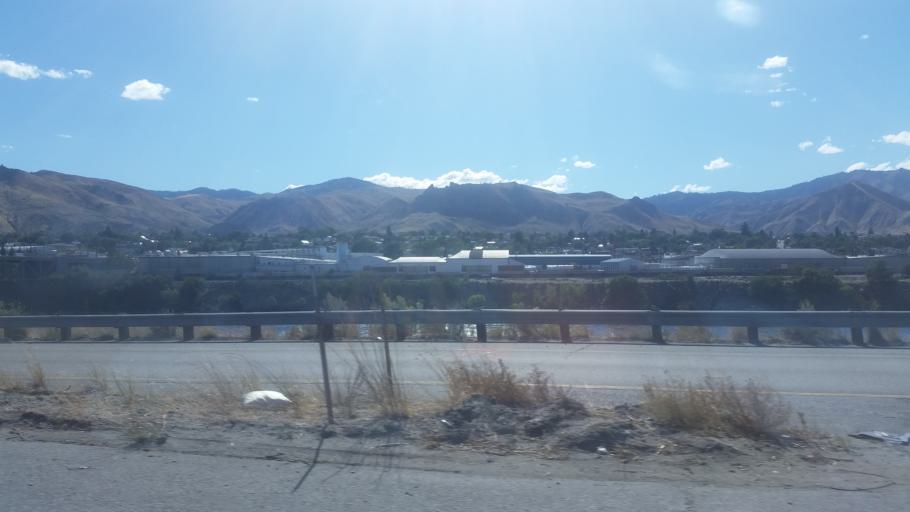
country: US
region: Washington
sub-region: Douglas County
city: East Wenatchee
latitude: 47.4130
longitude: -120.2940
